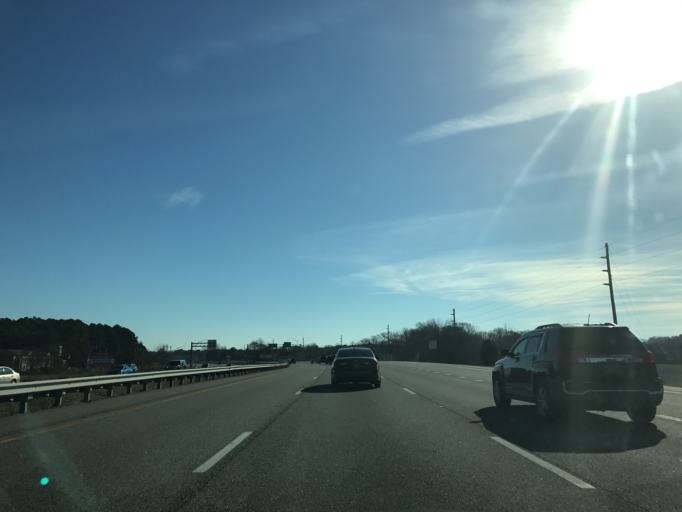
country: US
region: Maryland
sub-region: Queen Anne's County
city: Grasonville
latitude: 38.9619
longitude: -76.2089
